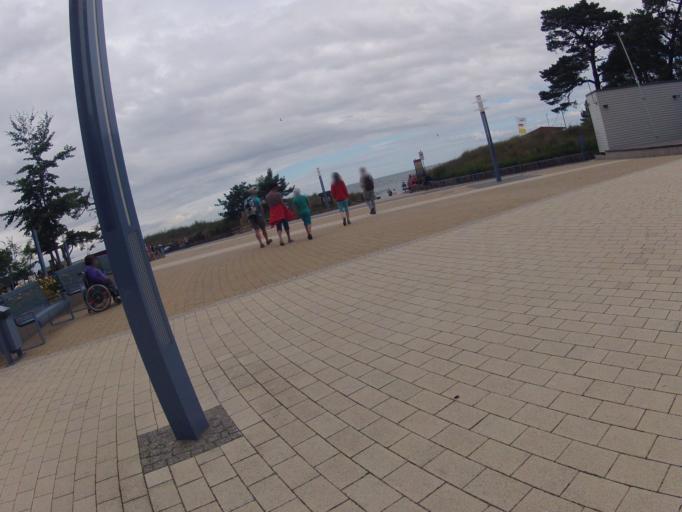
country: DE
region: Mecklenburg-Vorpommern
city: Ostseebad Zinnowitz
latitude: 54.0708
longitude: 13.9536
